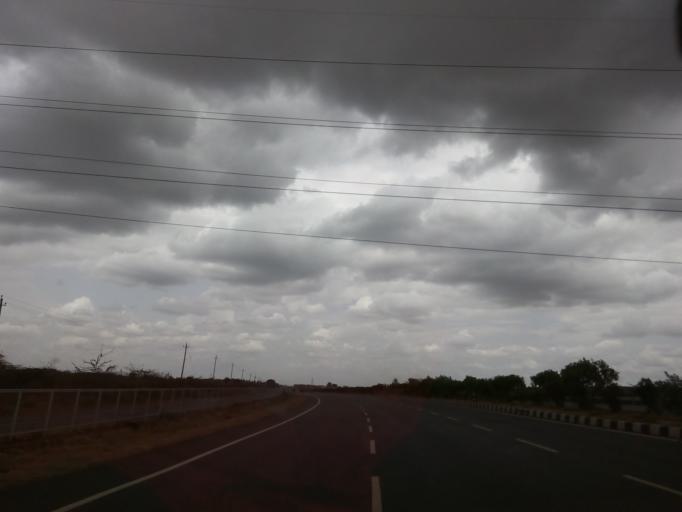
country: IN
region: Karnataka
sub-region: Chitradurga
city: Hiriyur
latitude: 13.9940
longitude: 76.5898
